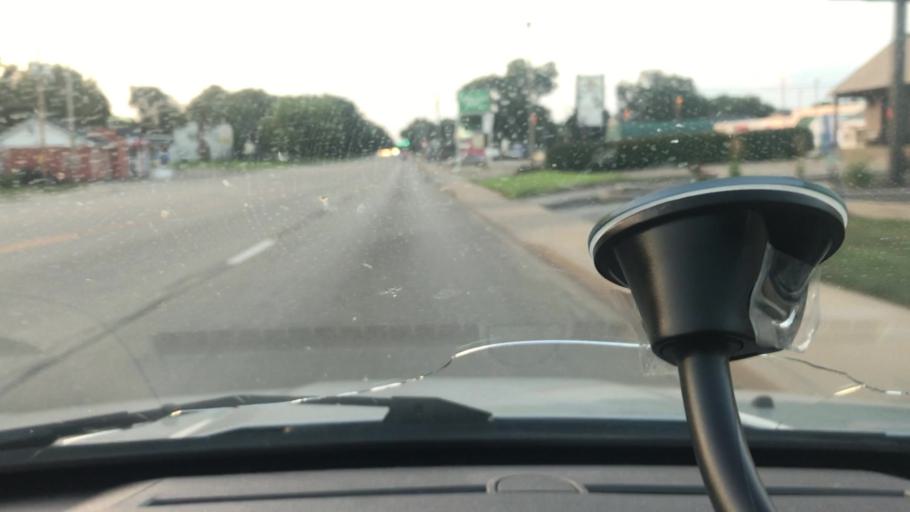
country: US
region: Illinois
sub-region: Tazewell County
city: Pekin
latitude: 40.5779
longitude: -89.6407
